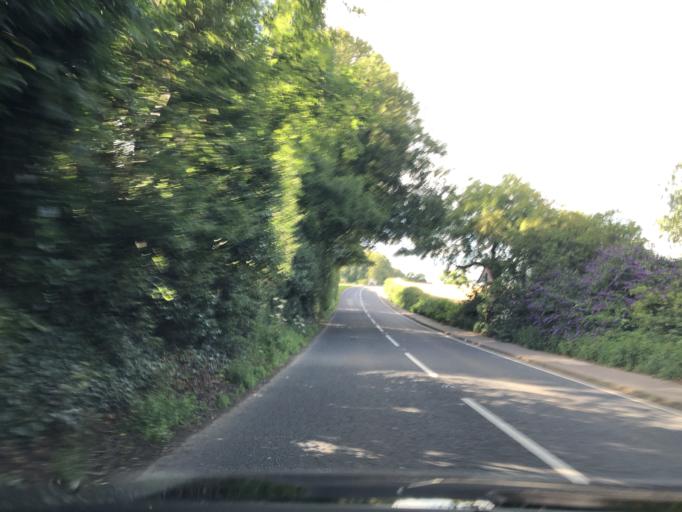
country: GB
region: Northern Ireland
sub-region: Ards District
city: Comber
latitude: 54.5606
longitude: -5.7620
